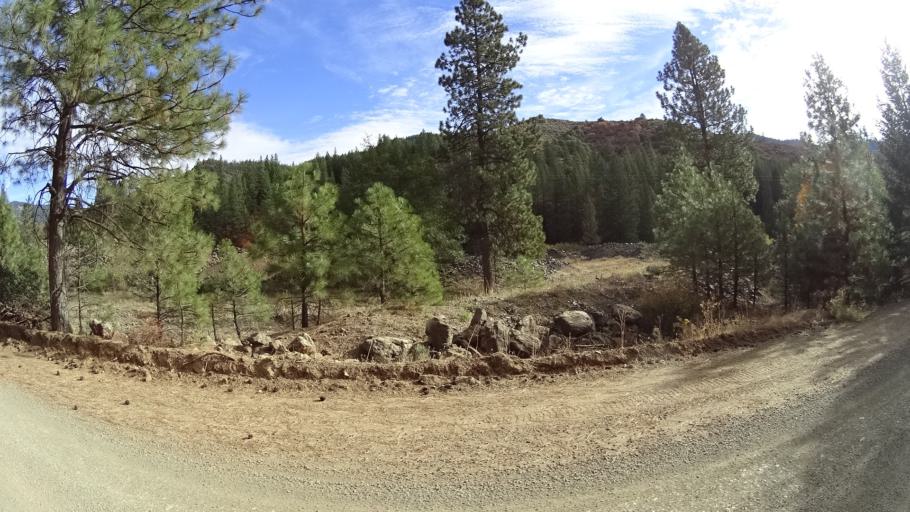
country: US
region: California
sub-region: Siskiyou County
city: Yreka
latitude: 41.6938
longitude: -122.8190
